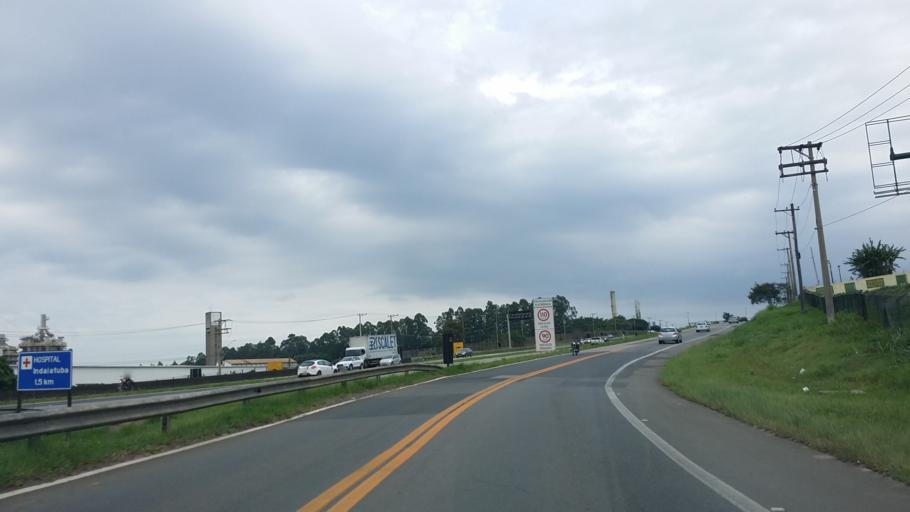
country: BR
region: Sao Paulo
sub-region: Indaiatuba
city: Indaiatuba
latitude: -23.1135
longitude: -47.2131
